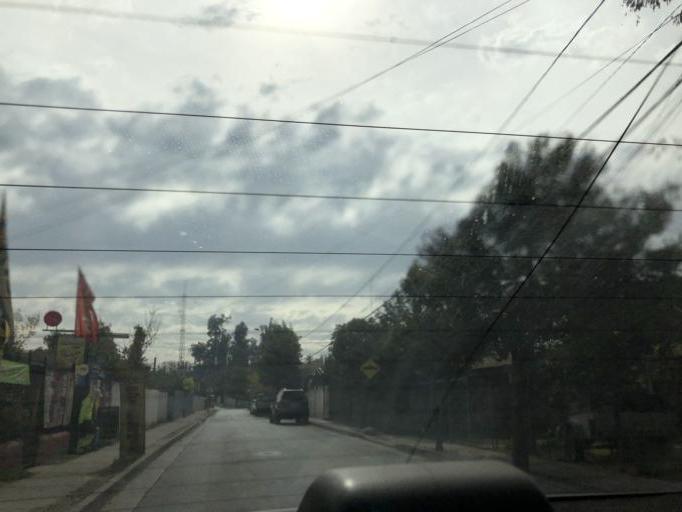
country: CL
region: Santiago Metropolitan
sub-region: Provincia de Cordillera
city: Puente Alto
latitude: -33.6093
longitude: -70.5368
